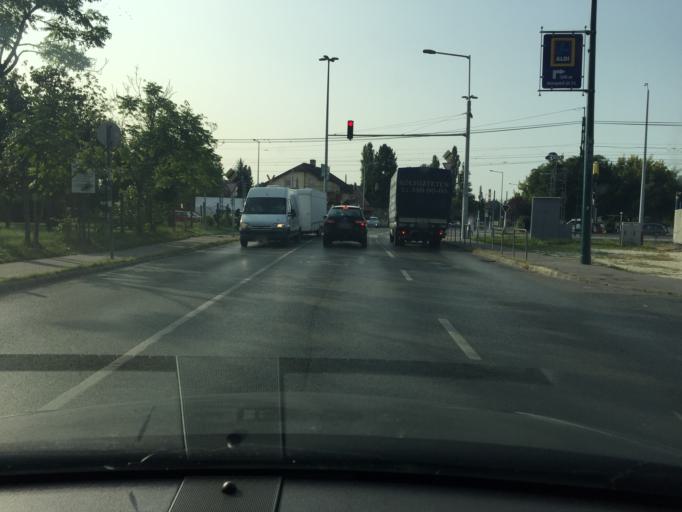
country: HU
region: Budapest
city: Budapest XVI. keruelet
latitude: 47.5056
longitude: 19.1521
